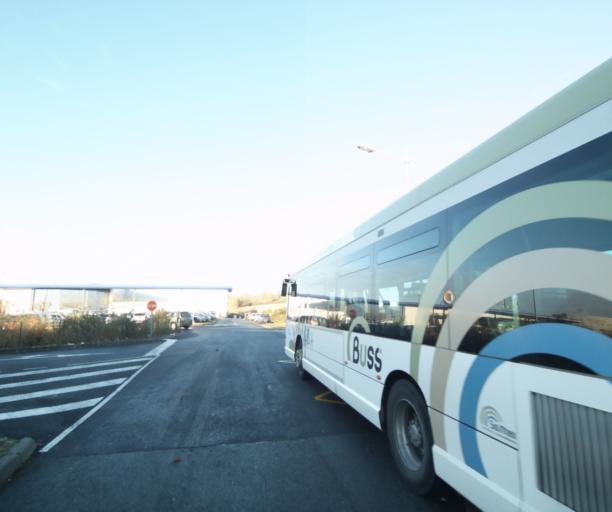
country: FR
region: Poitou-Charentes
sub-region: Departement de la Charente-Maritime
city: Saintes
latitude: 45.7482
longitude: -0.6760
